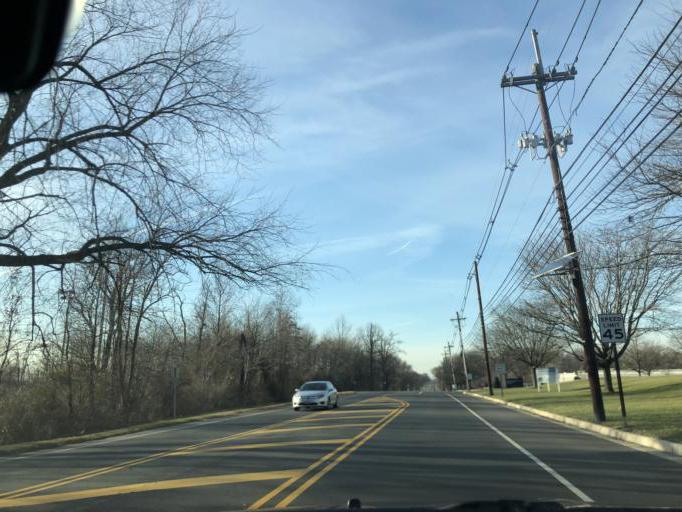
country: US
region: New Jersey
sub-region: Burlington County
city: Moorestown-Lenola
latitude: 39.9745
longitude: -74.9790
